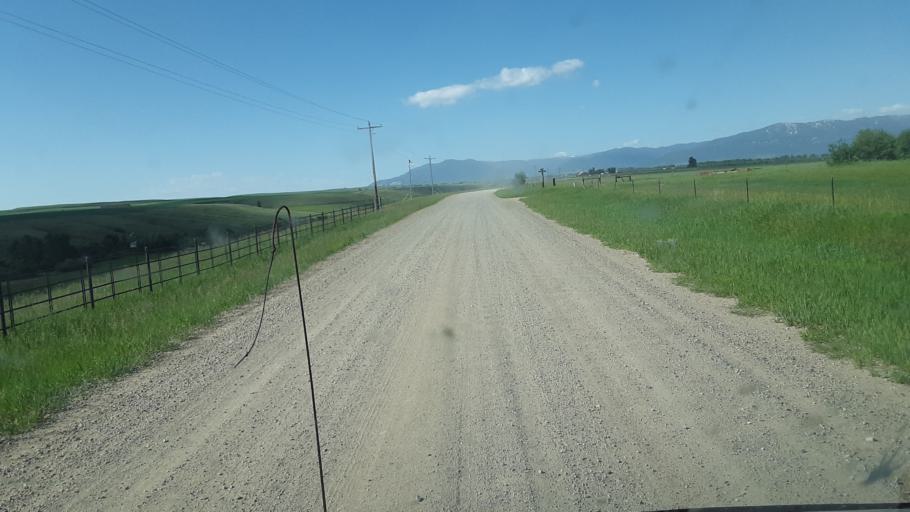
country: US
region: Montana
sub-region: Carbon County
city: Red Lodge
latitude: 45.3449
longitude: -109.1568
